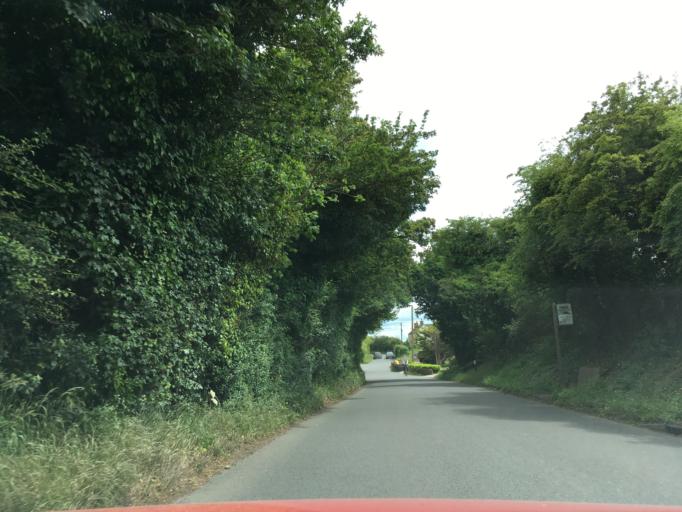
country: GB
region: England
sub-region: Wiltshire
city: Purton
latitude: 51.5688
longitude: -1.8557
